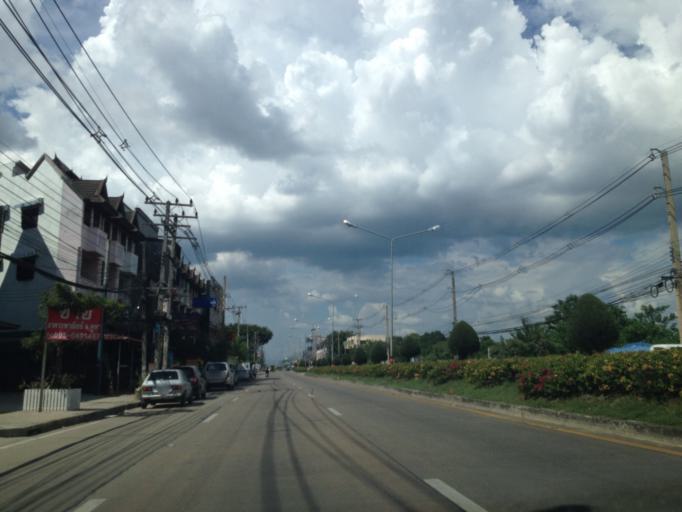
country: TH
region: Chiang Mai
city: Hang Dong
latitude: 18.7316
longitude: 98.9515
